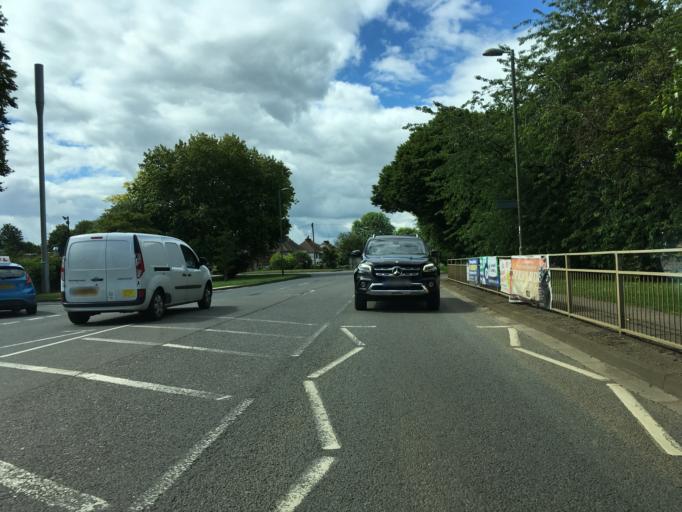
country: GB
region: England
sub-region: Oxfordshire
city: Banbury
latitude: 52.0526
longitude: -1.3461
